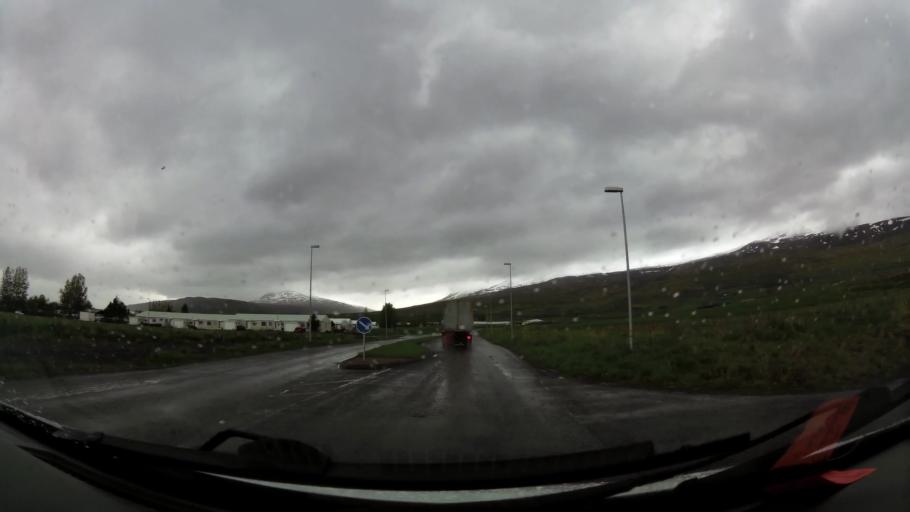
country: IS
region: Northeast
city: Akureyri
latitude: 65.6988
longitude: -18.1423
